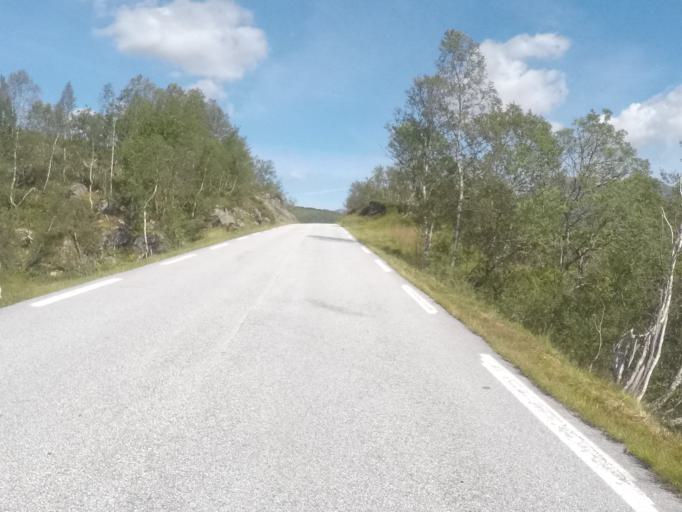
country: NO
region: Sogn og Fjordane
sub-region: Balestrand
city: Balestrand
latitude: 61.3348
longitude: 6.3884
